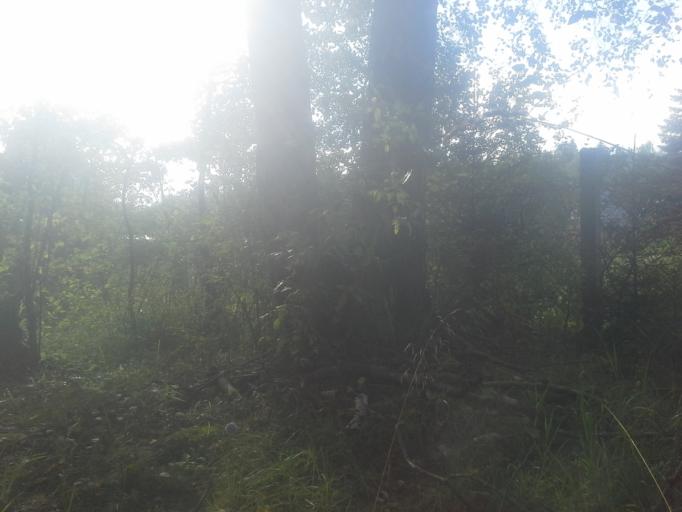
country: RU
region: Moskovskaya
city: Kievskij
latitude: 55.3475
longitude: 36.9571
